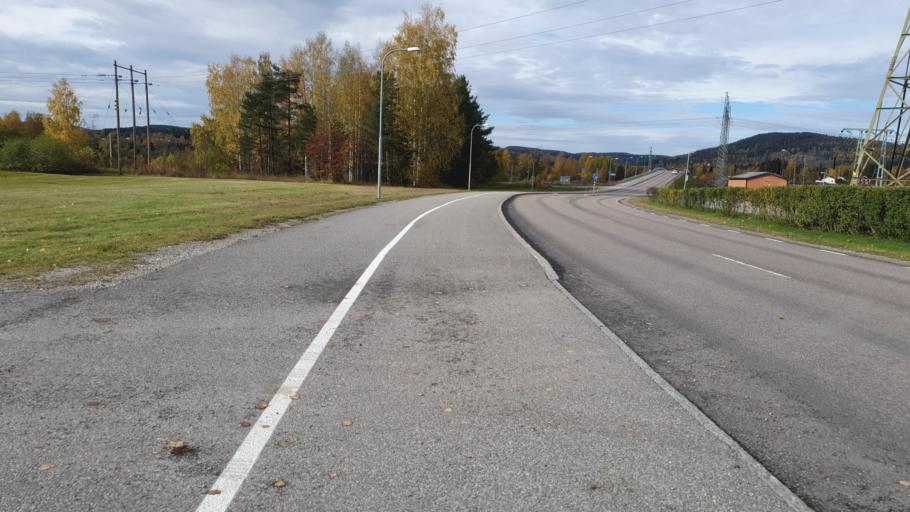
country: SE
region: Vaesternorrland
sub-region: Sundsvalls Kommun
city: Sundsvall
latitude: 62.4054
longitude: 17.2389
